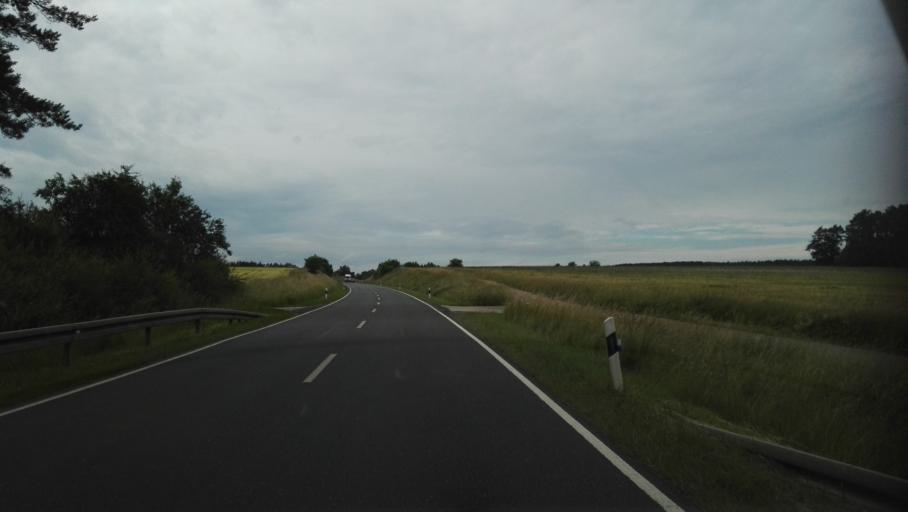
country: DE
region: Bavaria
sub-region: Upper Franconia
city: Hollfeld
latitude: 49.9188
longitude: 11.3097
